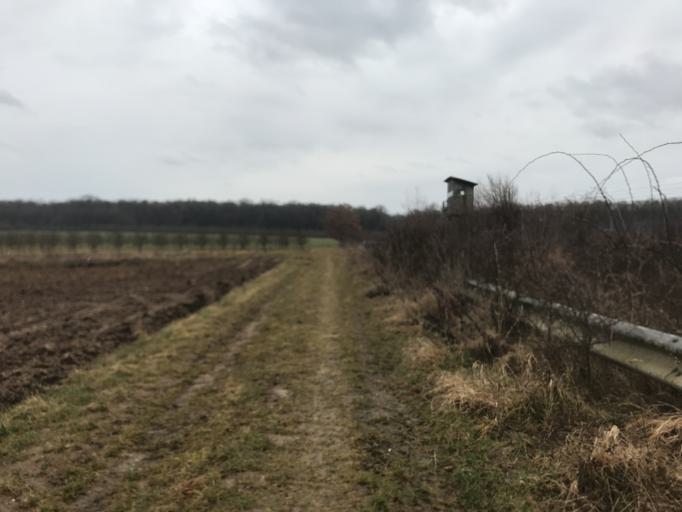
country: DE
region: Rheinland-Pfalz
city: Essenheim
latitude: 49.9693
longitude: 8.1647
